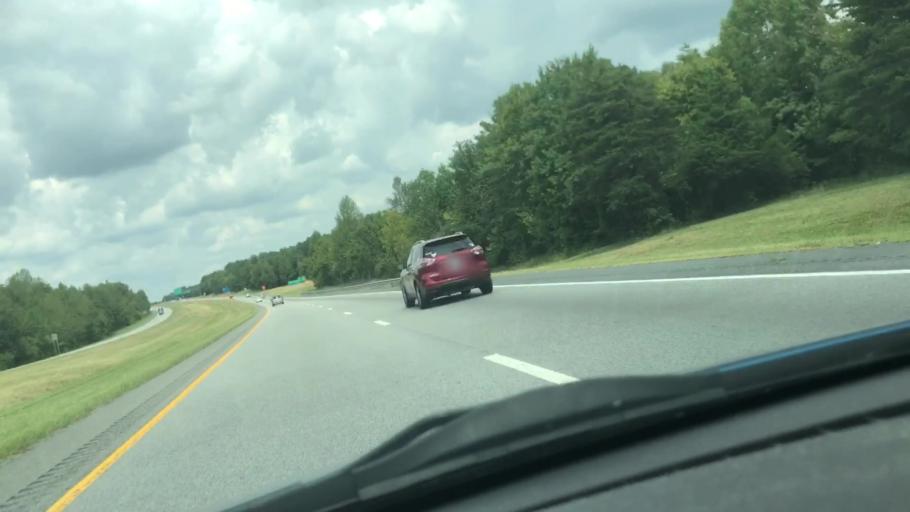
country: US
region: North Carolina
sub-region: Guilford County
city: Pleasant Garden
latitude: 35.9748
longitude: -79.8213
